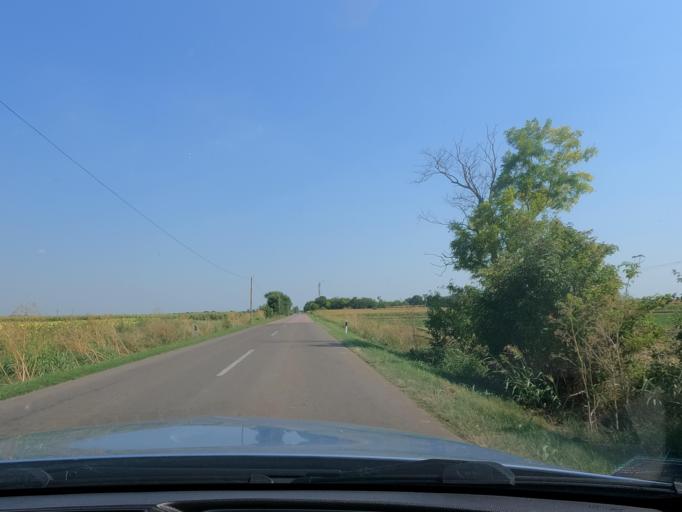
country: RS
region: Autonomna Pokrajina Vojvodina
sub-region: Severnobacki Okrug
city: Mali Igos
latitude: 45.7725
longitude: 19.7322
